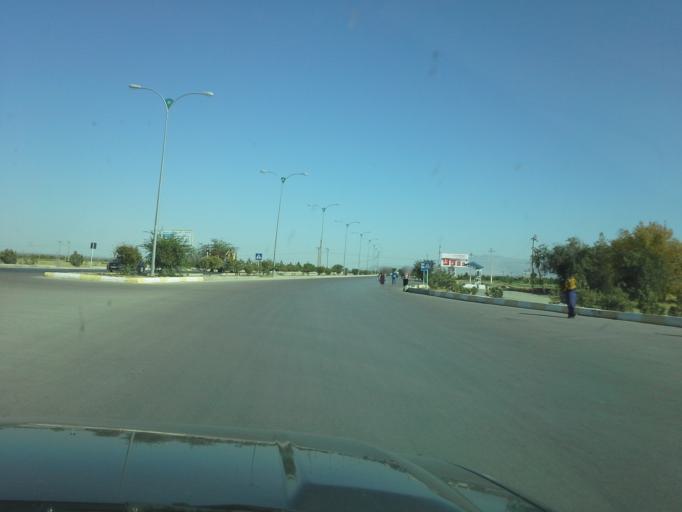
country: TM
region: Ahal
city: Baharly
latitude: 38.4215
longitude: 57.4388
